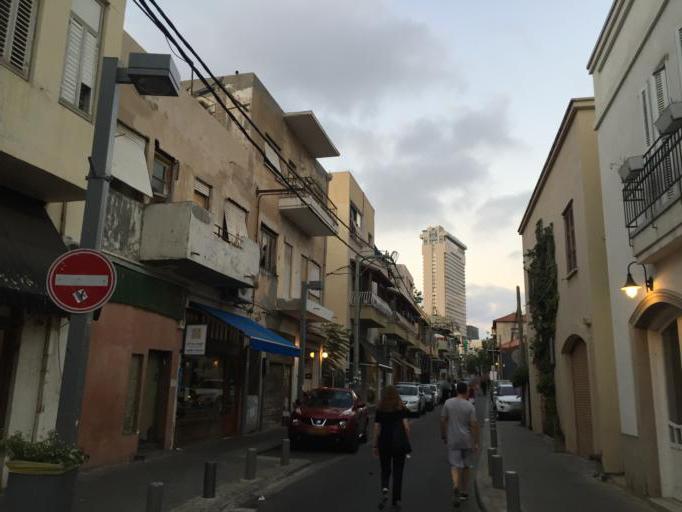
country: IL
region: Tel Aviv
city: Yafo
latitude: 32.0622
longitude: 34.7648
